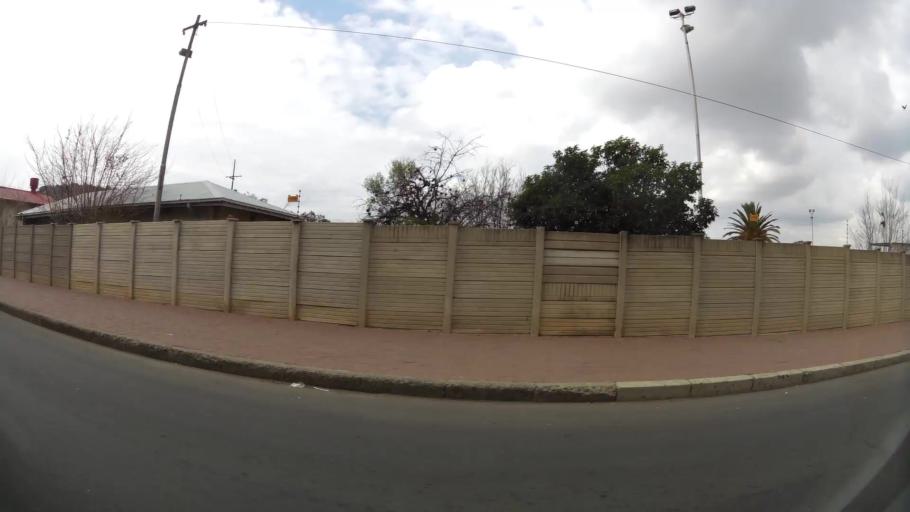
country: ZA
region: Orange Free State
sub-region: Mangaung Metropolitan Municipality
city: Bloemfontein
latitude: -29.1107
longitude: 26.2199
